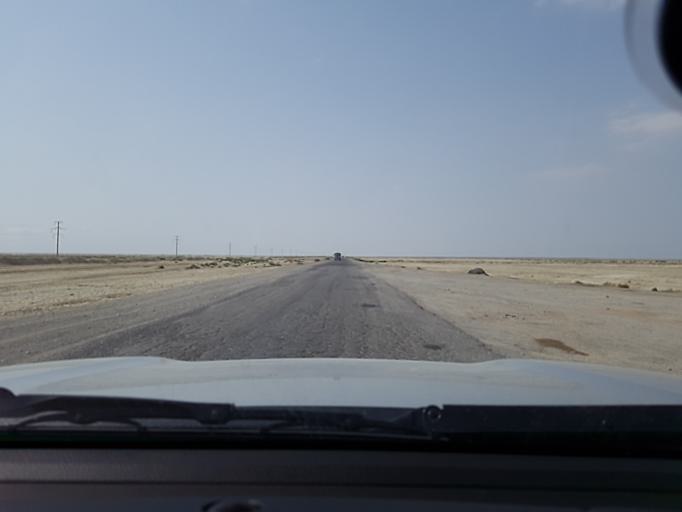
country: TM
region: Balkan
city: Gumdag
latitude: 38.9958
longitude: 54.5864
